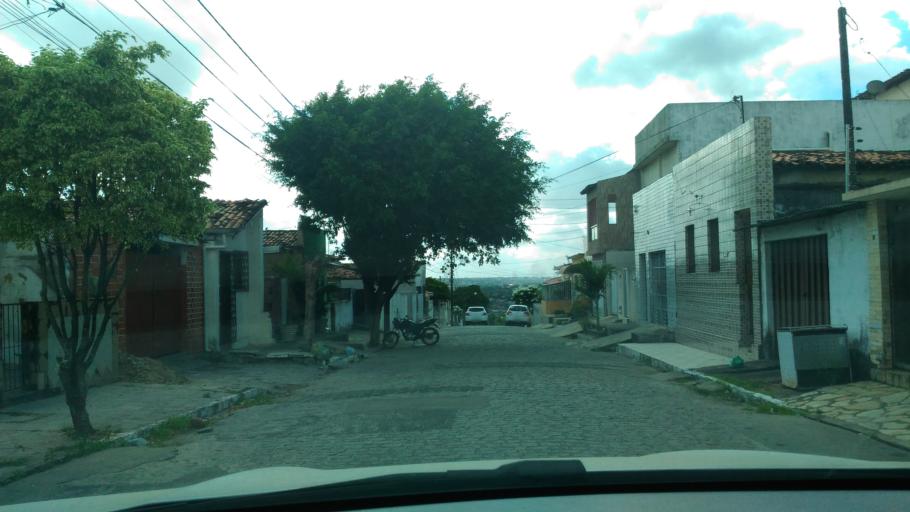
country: BR
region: Paraiba
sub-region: Joao Pessoa
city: Joao Pessoa
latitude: -7.1241
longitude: -34.8878
